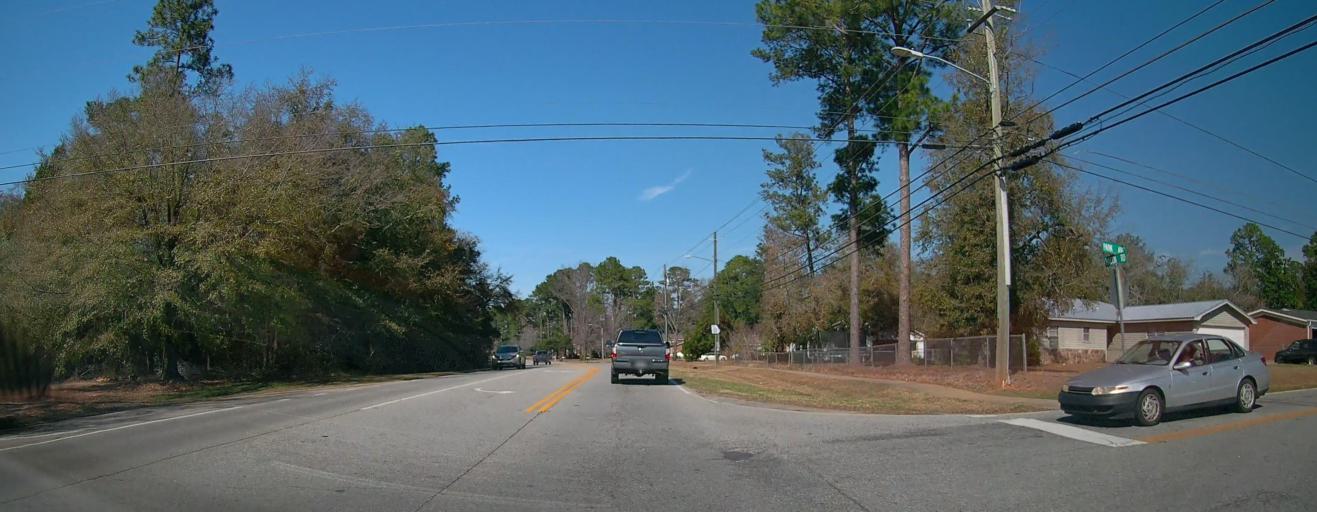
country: US
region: Georgia
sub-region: Houston County
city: Perry
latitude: 32.4700
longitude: -83.7289
